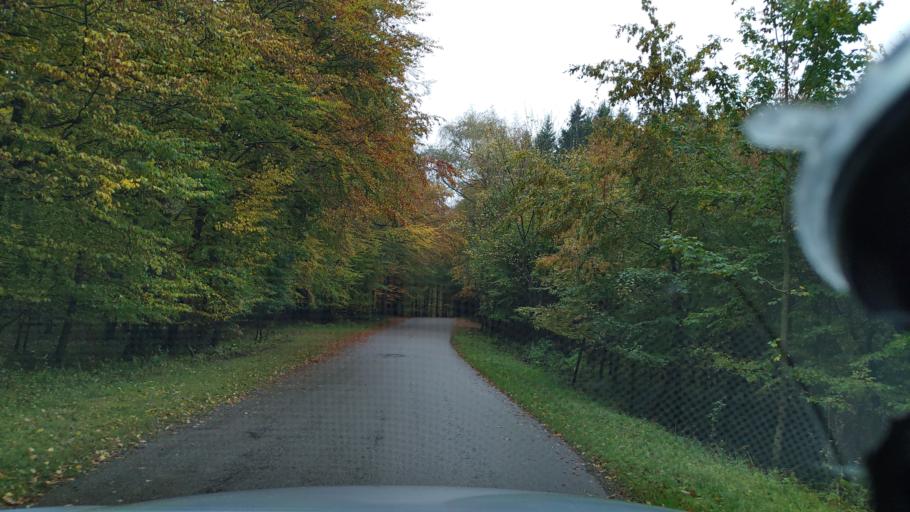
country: DK
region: Zealand
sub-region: Faxe Kommune
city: Ronnede
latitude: 55.2492
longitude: 11.9564
